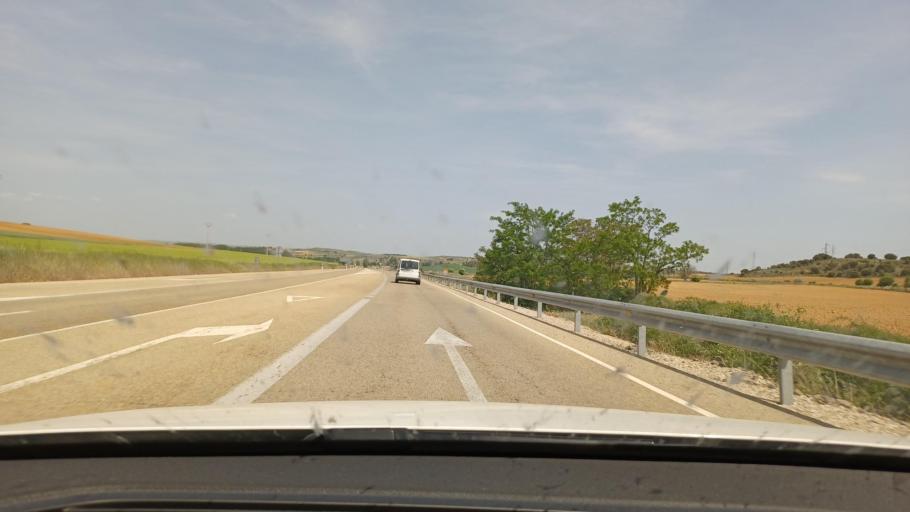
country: ES
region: Castille and Leon
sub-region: Provincia de Soria
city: Barca
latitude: 41.4651
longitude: -2.6330
